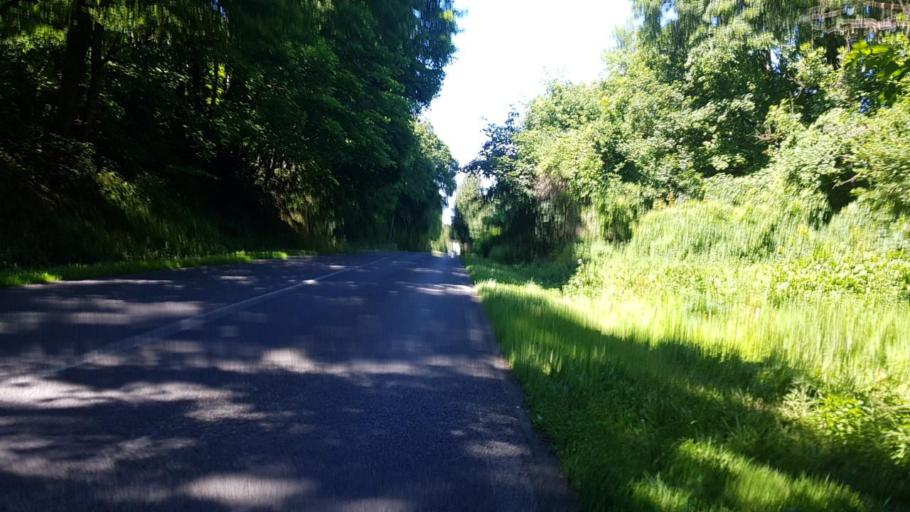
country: FR
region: Ile-de-France
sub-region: Departement de Seine-et-Marne
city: Chamigny
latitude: 48.9646
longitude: 3.1592
